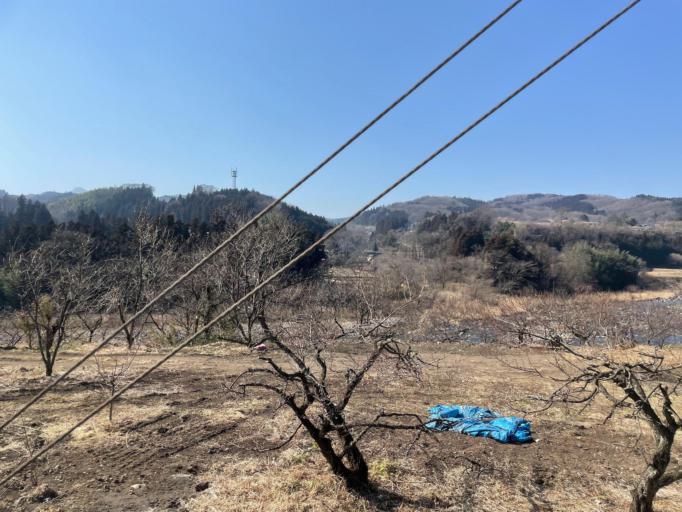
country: JP
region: Gunma
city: Nakanojomachi
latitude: 36.5674
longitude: 138.8881
